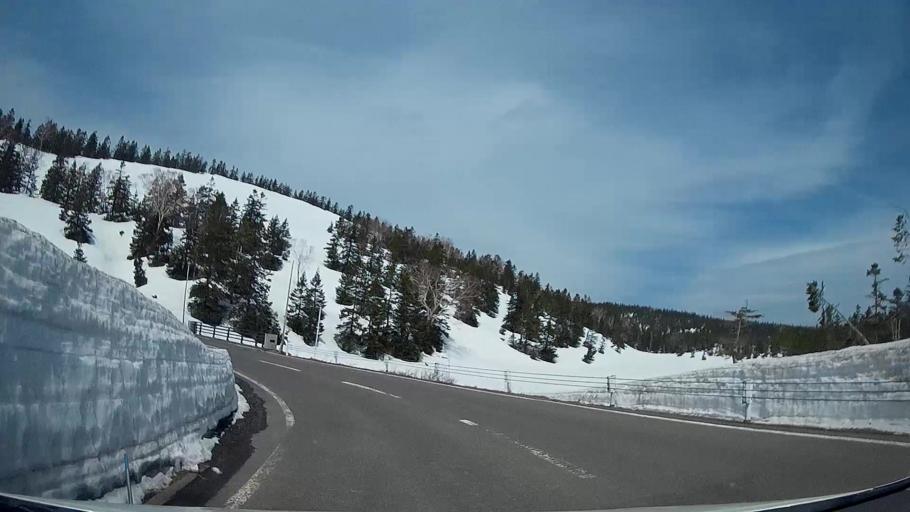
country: JP
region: Akita
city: Hanawa
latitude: 39.9546
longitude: 140.8852
